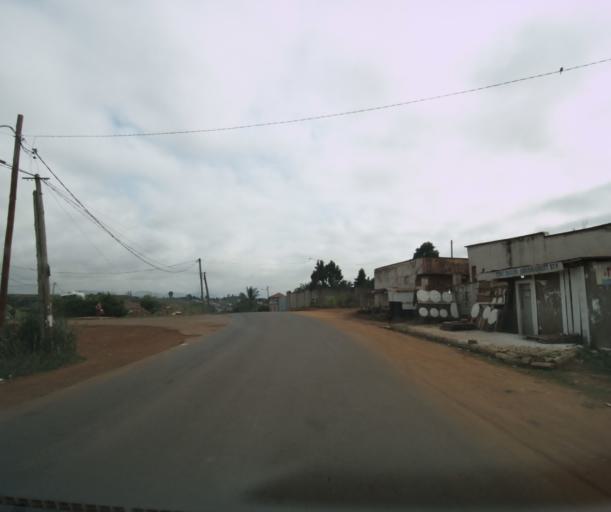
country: CM
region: Centre
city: Yaounde
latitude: 3.8026
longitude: 11.5223
